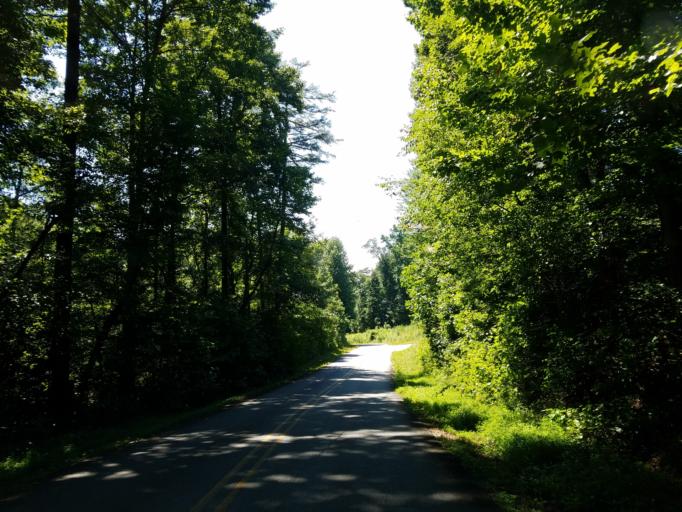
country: US
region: Georgia
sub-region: Lumpkin County
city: Dahlonega
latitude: 34.4151
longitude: -83.9994
